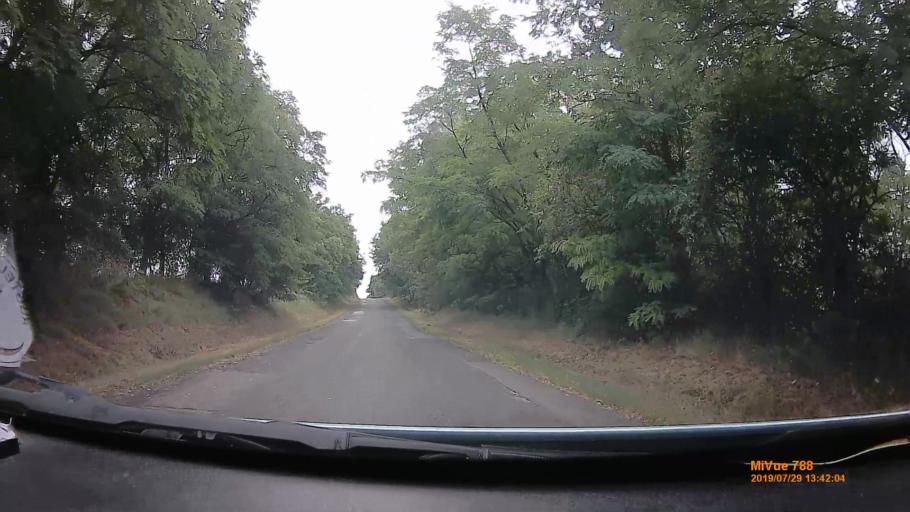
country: HU
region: Somogy
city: Balatonfoldvar
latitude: 46.8110
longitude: 17.9258
